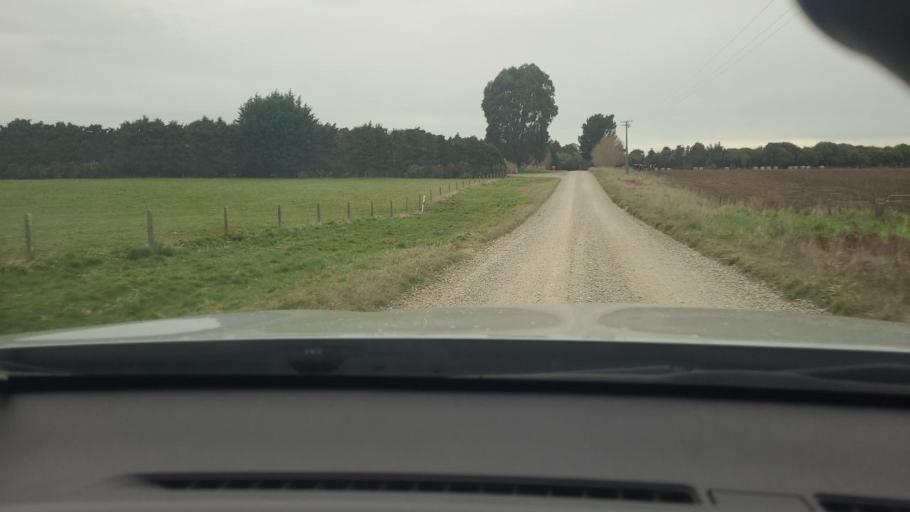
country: NZ
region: Southland
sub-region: Invercargill City
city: Invercargill
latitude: -46.2732
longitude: 168.5133
